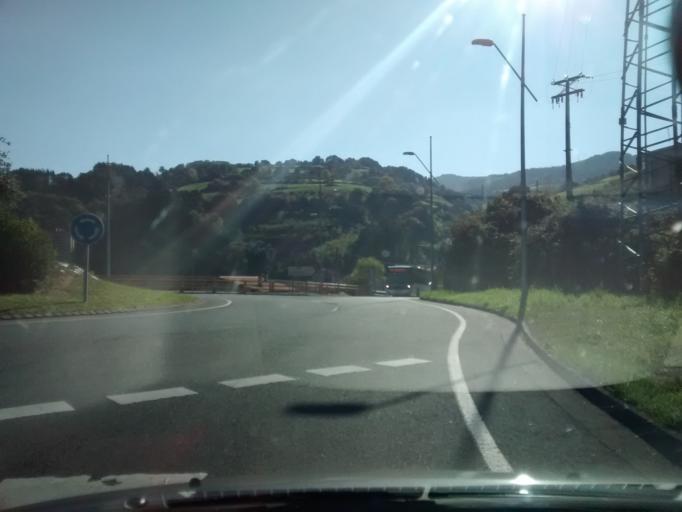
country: ES
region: Basque Country
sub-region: Provincia de Guipuzcoa
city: Deba
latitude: 43.2911
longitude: -2.3640
